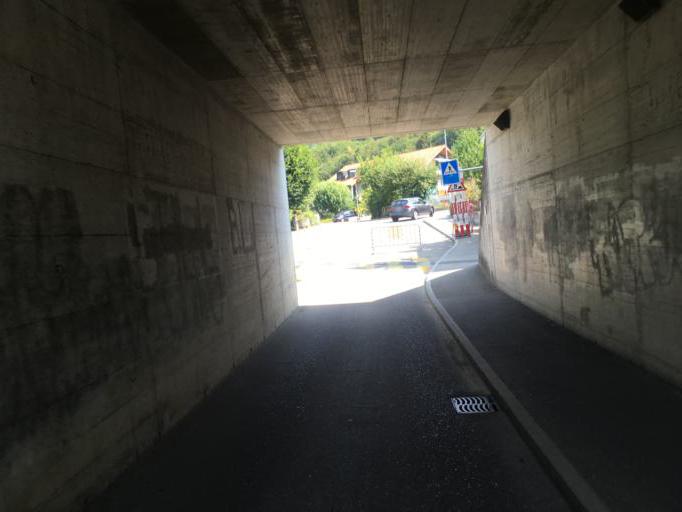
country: CH
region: Bern
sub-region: Bern-Mittelland District
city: Muri
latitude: 46.9379
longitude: 7.4987
